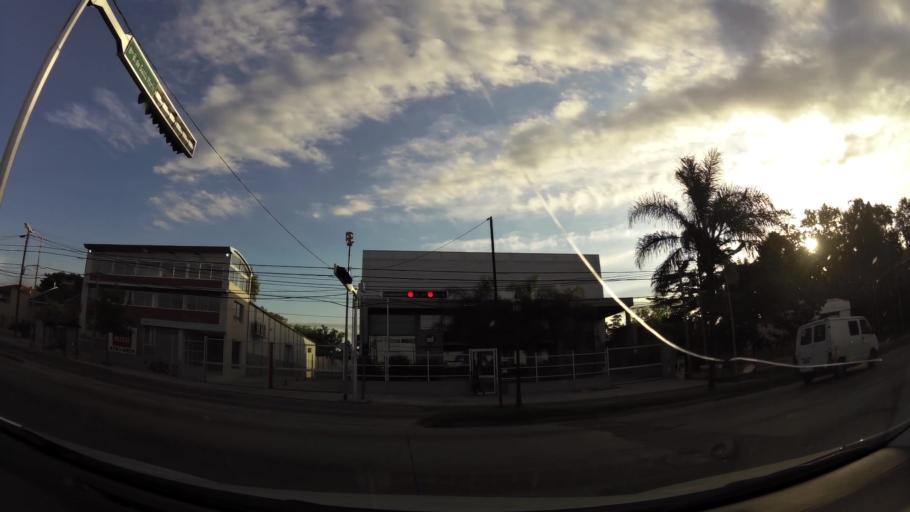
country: AR
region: Buenos Aires
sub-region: Partido de Tigre
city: Tigre
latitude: -34.4509
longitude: -58.6576
